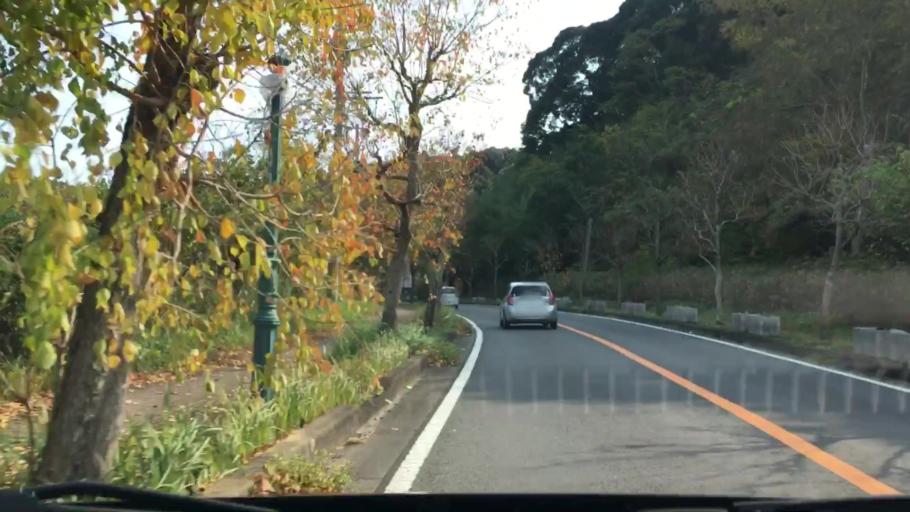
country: JP
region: Nagasaki
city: Togitsu
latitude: 32.9873
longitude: 129.7673
